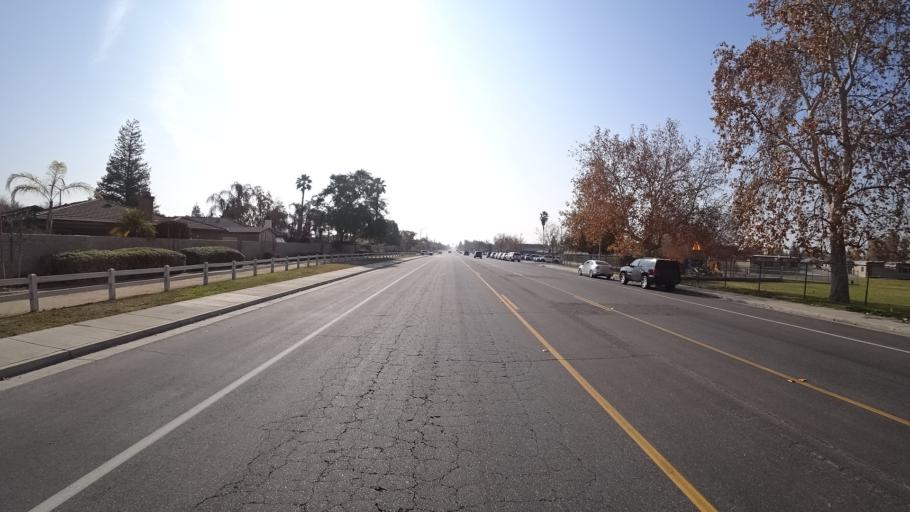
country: US
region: California
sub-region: Kern County
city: Greenacres
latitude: 35.4087
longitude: -119.1188
